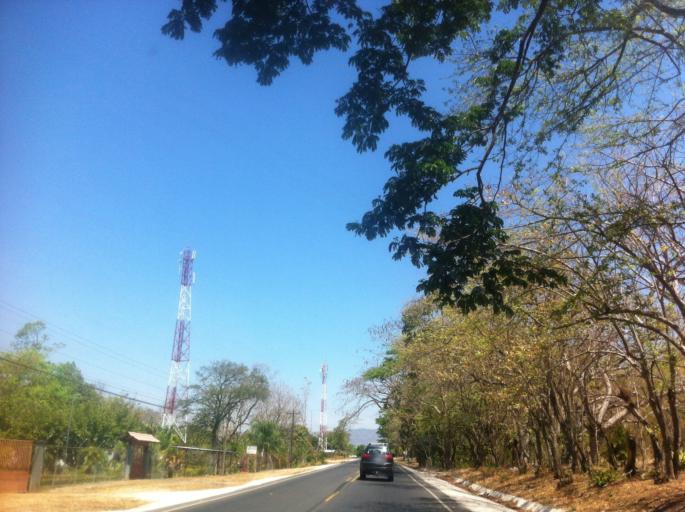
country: CR
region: Guanacaste
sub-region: Canton de Nicoya
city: Nicoya
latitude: 10.1764
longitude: -85.4614
